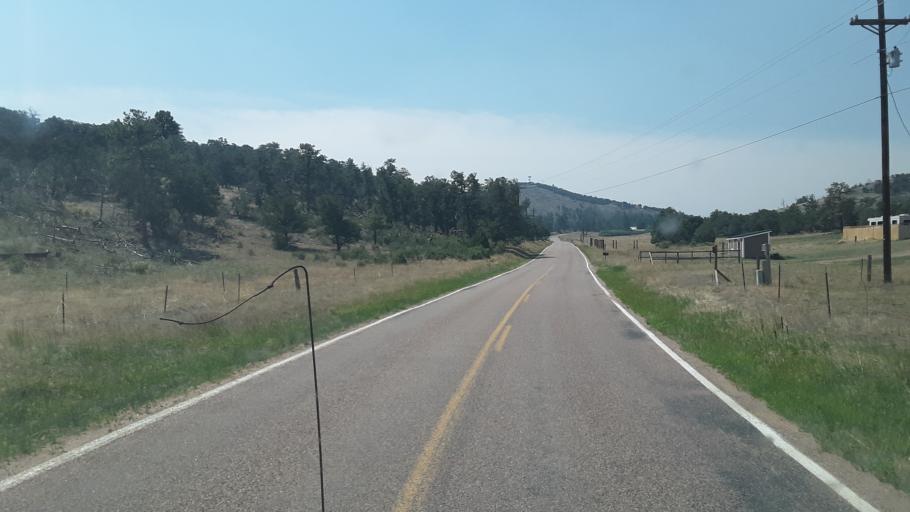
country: US
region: Colorado
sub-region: Custer County
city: Westcliffe
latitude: 38.3346
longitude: -105.4850
